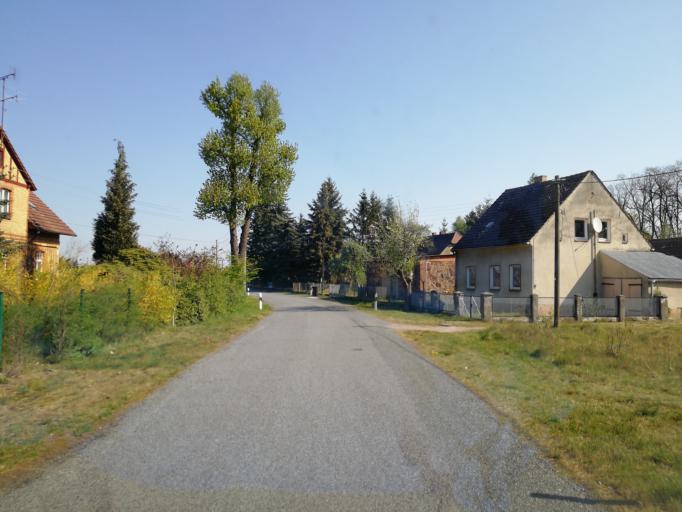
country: DE
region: Brandenburg
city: Bronkow
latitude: 51.6960
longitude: 13.8724
